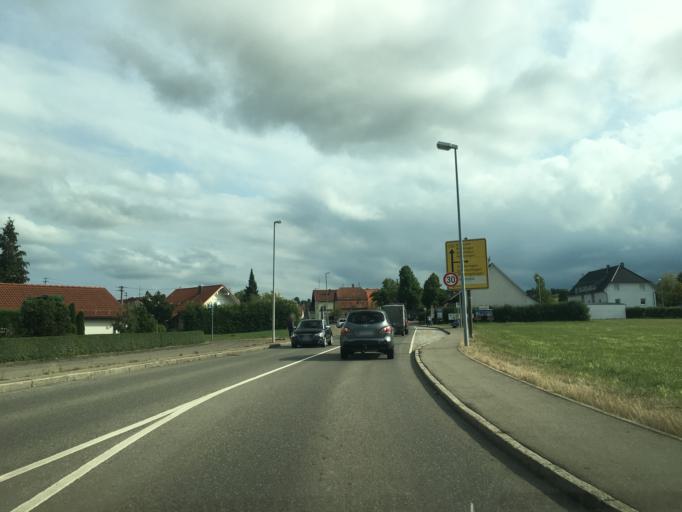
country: DE
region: Baden-Wuerttemberg
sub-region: Tuebingen Region
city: Sankt Johann
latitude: 48.3895
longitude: 9.2924
